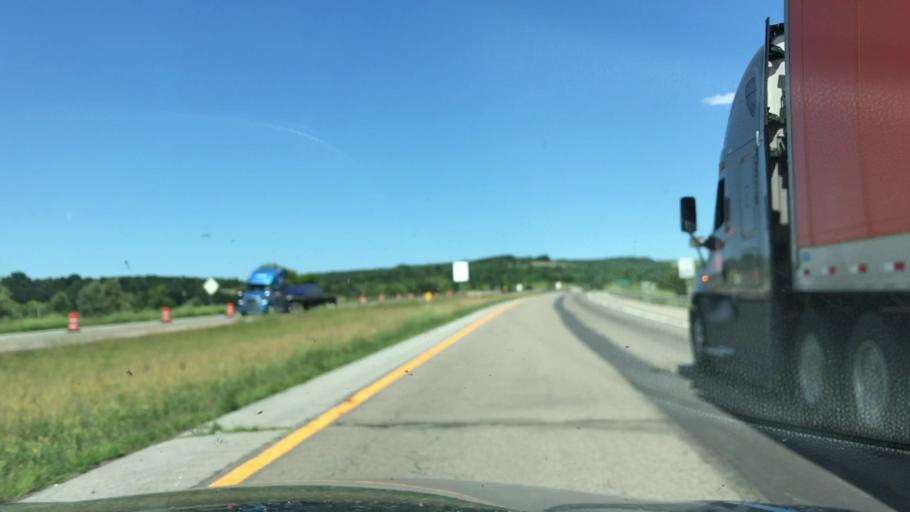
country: US
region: New York
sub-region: Steuben County
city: Wayland
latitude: 42.5413
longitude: -77.5958
